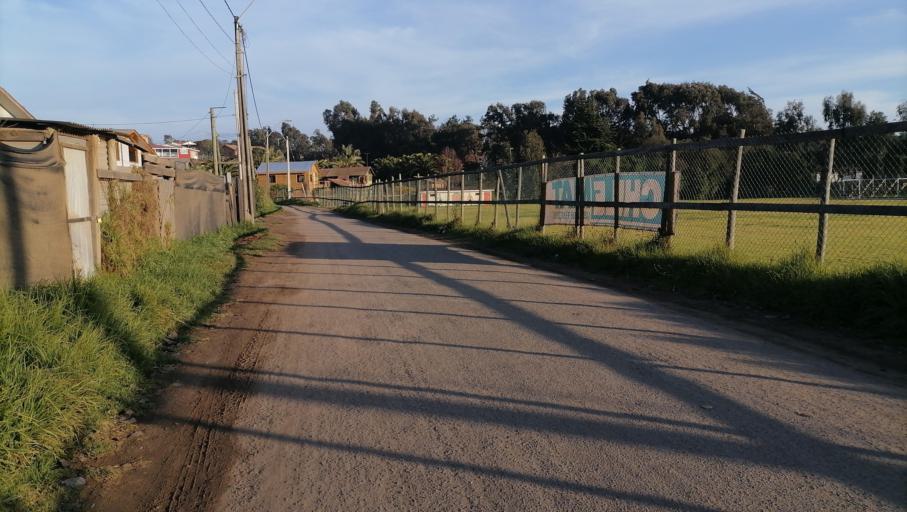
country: CL
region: Valparaiso
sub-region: Provincia de Valparaiso
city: Vina del Mar
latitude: -32.9013
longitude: -71.4960
